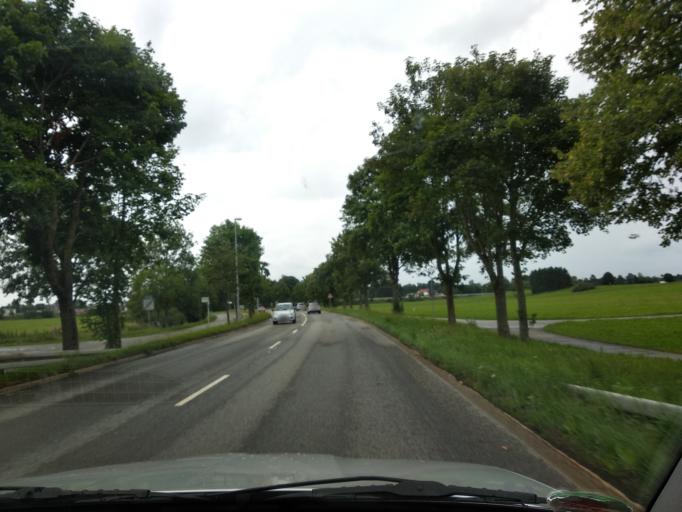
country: DE
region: Baden-Wuerttemberg
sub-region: Tuebingen Region
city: Leutkirch im Allgau
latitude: 47.8276
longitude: 10.0057
